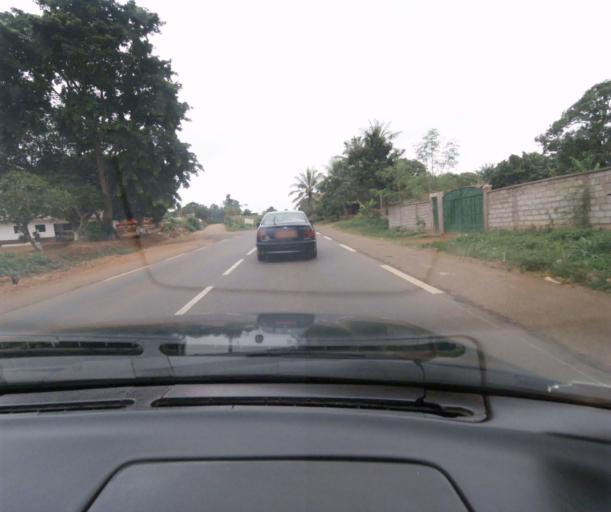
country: CM
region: Centre
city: Obala
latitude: 4.1715
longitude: 11.4788
